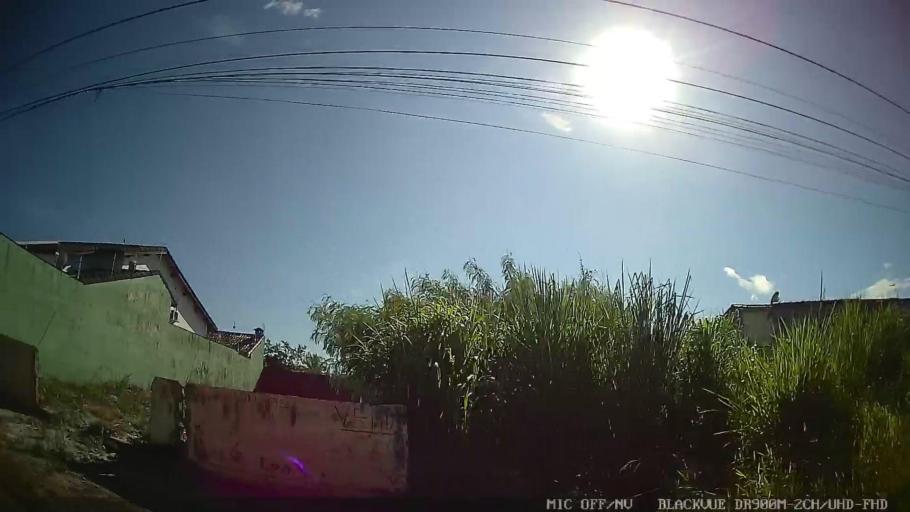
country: BR
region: Sao Paulo
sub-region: Peruibe
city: Peruibe
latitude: -24.2769
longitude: -46.9476
